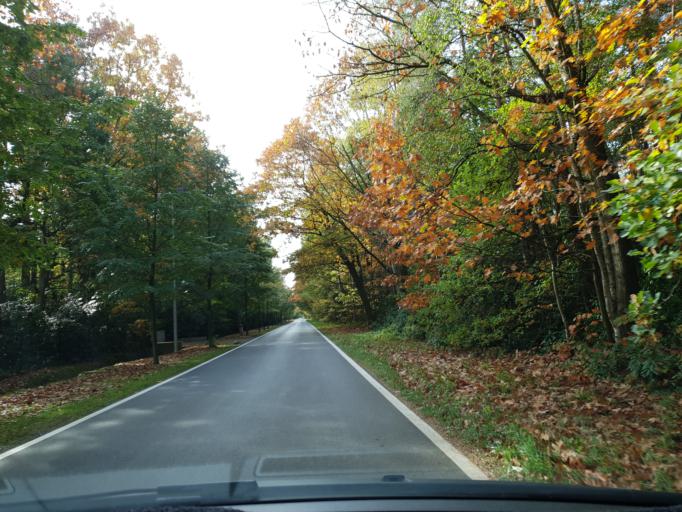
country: BE
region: Flanders
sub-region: Provincie Antwerpen
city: Kalmthout
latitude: 51.3587
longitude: 4.4428
